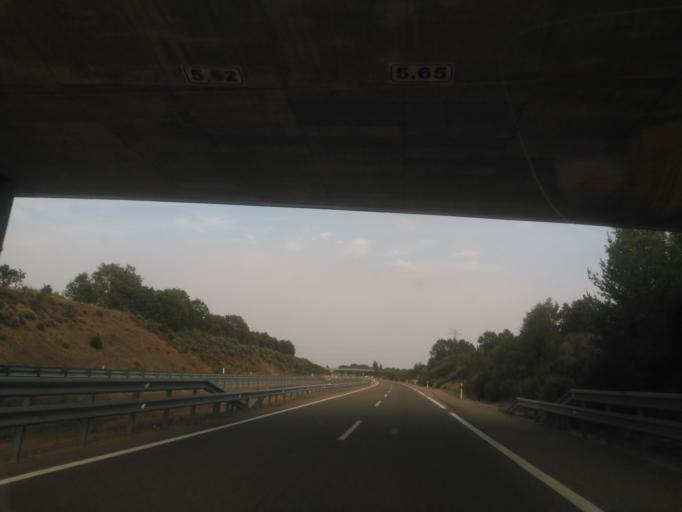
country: ES
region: Castille and Leon
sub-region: Provincia de Zamora
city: Cernadilla
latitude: 42.0318
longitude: -6.4253
